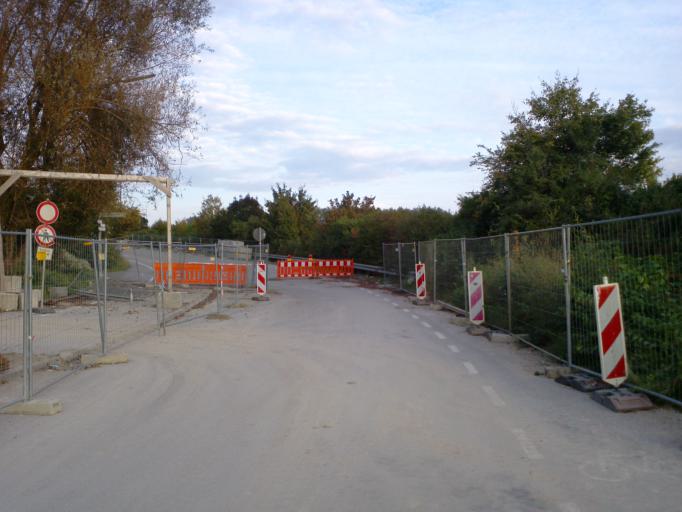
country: DE
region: Baden-Wuerttemberg
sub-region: Karlsruhe Region
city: Karlsruhe
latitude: 48.9896
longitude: 8.3930
